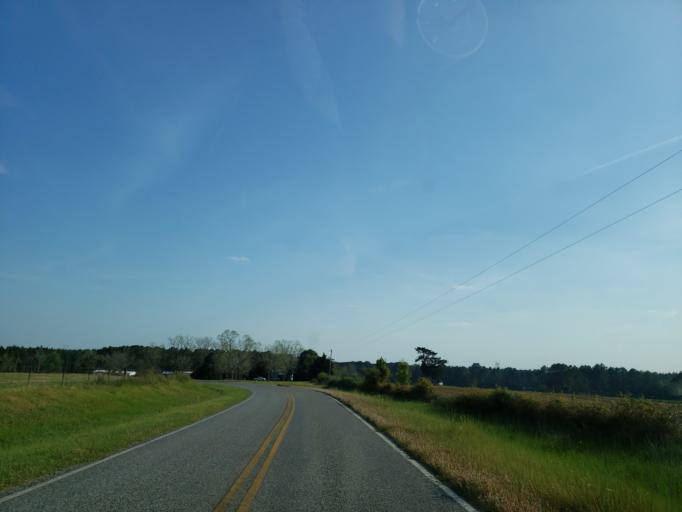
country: US
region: Georgia
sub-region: Tift County
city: Tifton
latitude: 31.5023
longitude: -83.5603
